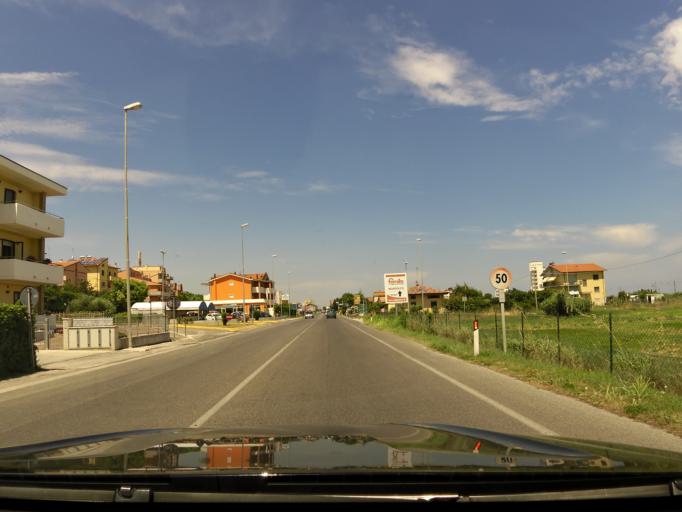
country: IT
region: The Marches
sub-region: Provincia di Pesaro e Urbino
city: Marotta
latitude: 43.7547
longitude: 13.1604
